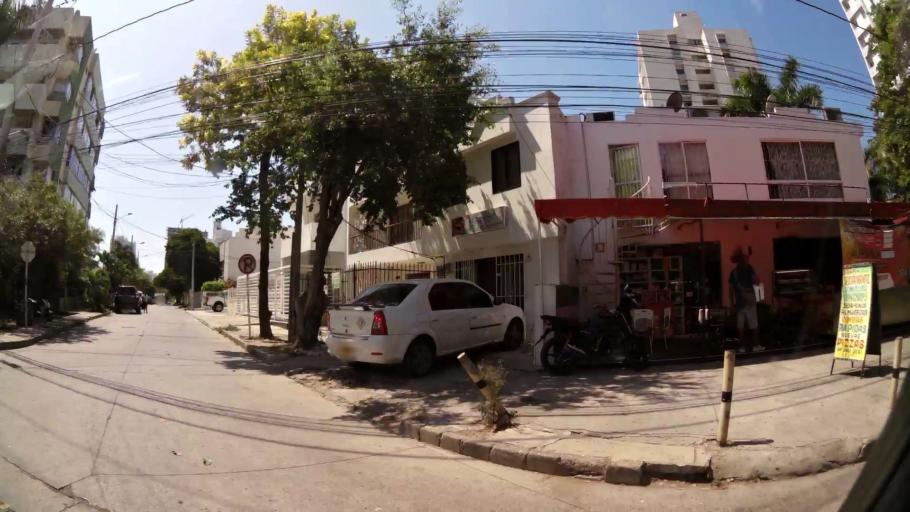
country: CO
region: Bolivar
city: Cartagena
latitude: 10.4190
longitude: -75.5336
